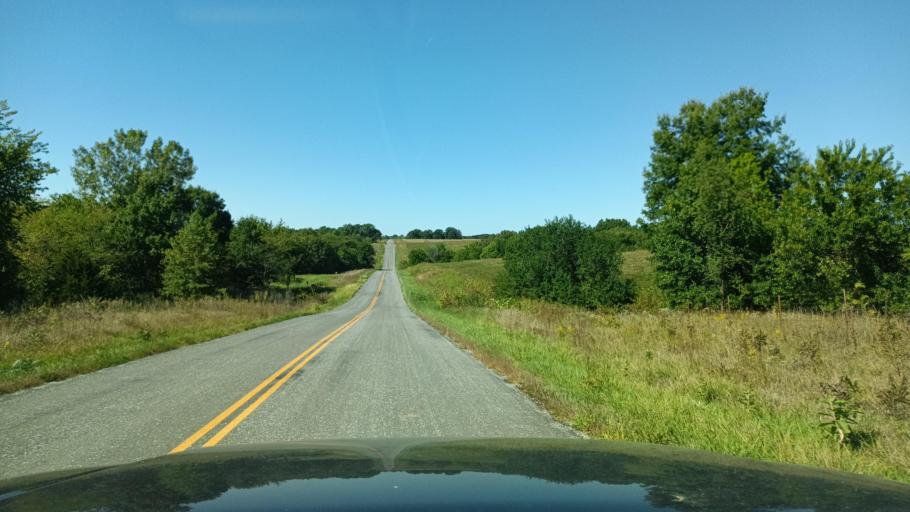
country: US
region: Missouri
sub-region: Adair County
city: Kirksville
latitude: 40.3303
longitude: -92.5316
